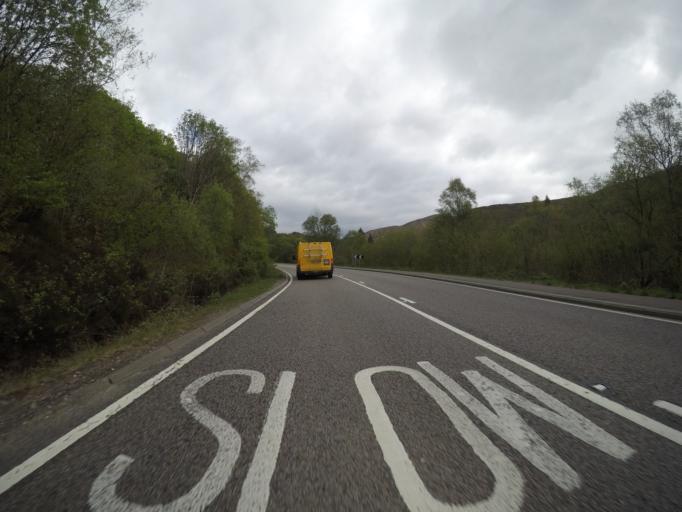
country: GB
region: Scotland
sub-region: Highland
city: Fort William
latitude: 56.7126
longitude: -5.2270
